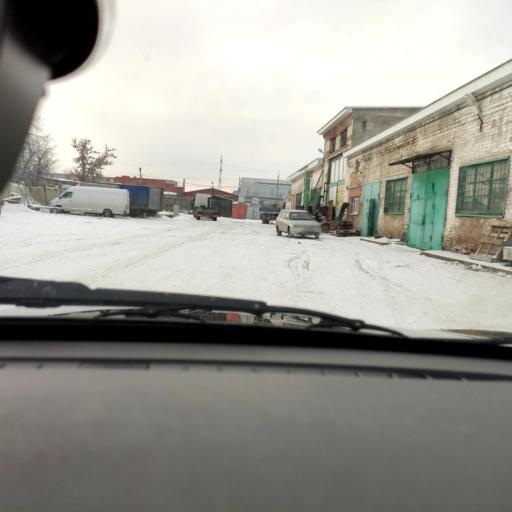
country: RU
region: Samara
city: Tol'yatti
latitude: 53.5328
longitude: 49.4471
